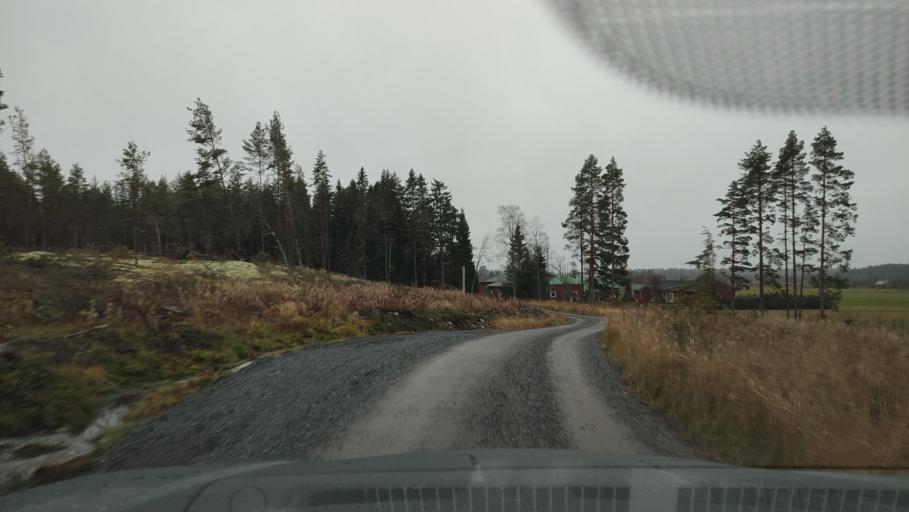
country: FI
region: Southern Ostrobothnia
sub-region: Suupohja
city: Karijoki
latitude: 62.2242
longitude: 21.5697
